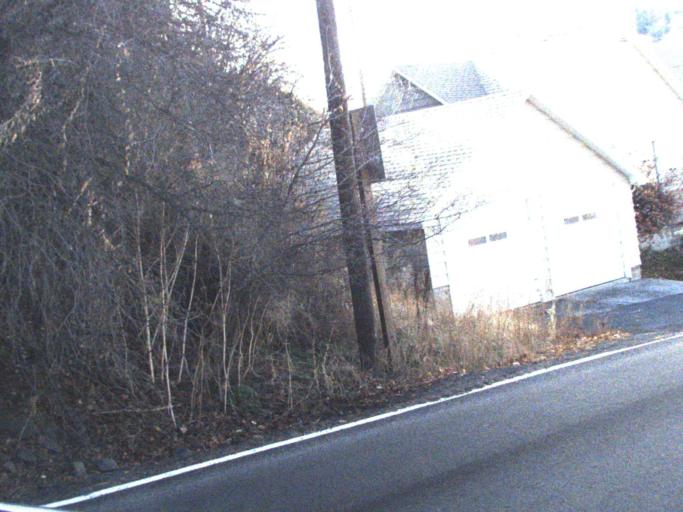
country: US
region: Washington
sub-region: Whitman County
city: Colfax
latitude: 46.8799
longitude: -117.3626
